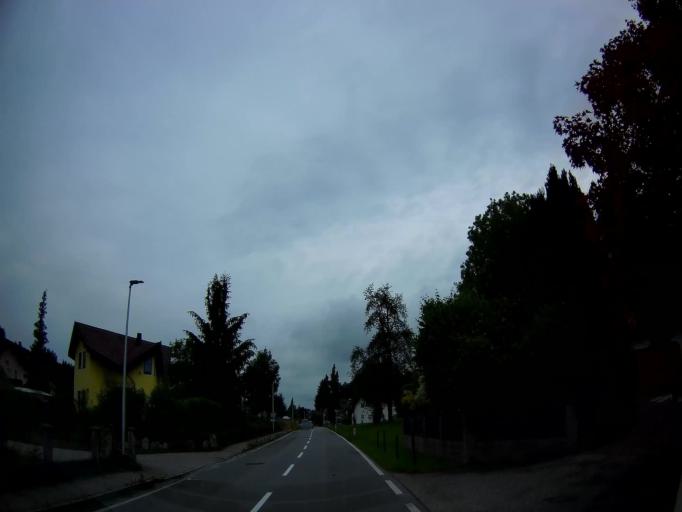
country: AT
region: Salzburg
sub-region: Politischer Bezirk Salzburg-Umgebung
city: Mattsee
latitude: 48.0865
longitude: 13.1478
